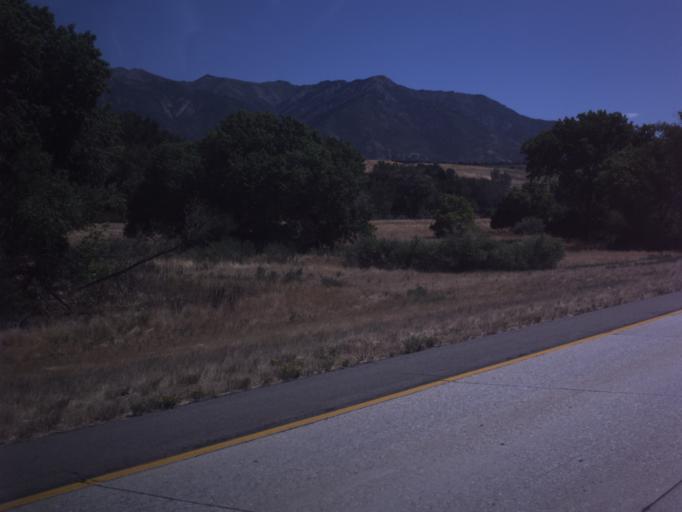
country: US
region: Utah
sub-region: Weber County
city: Washington Terrace
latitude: 41.1542
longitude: -111.9854
